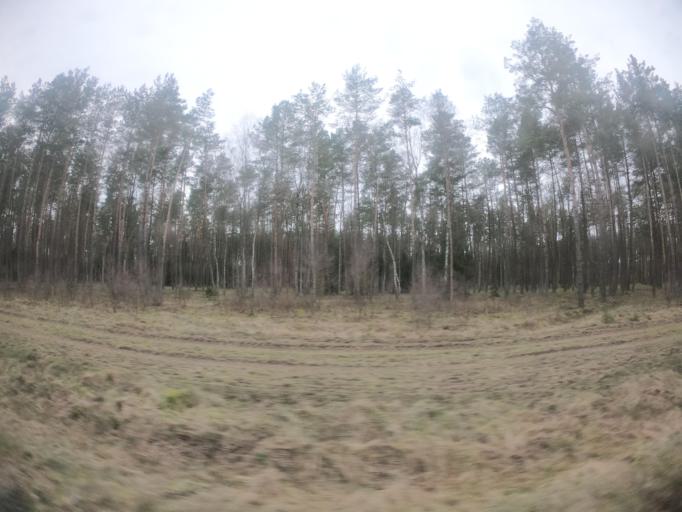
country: PL
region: Pomeranian Voivodeship
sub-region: Powiat czluchowski
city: Czarne
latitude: 53.7512
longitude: 16.8485
